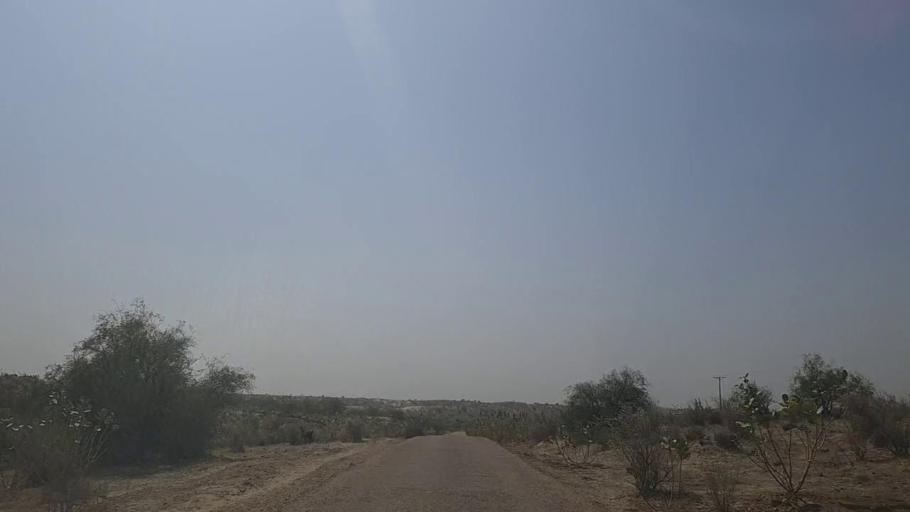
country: PK
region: Sindh
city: Naukot
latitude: 24.8249
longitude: 69.4830
